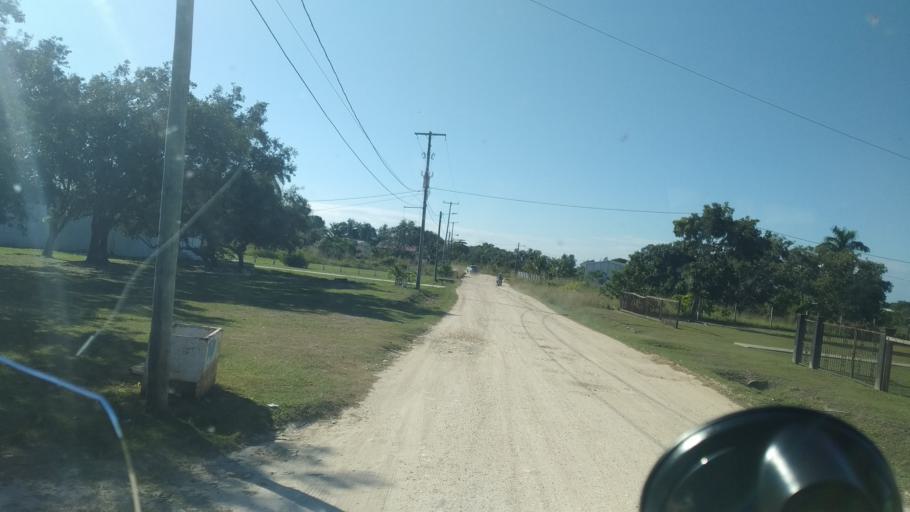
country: BZ
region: Belize
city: Belize City
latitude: 17.5533
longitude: -88.3261
